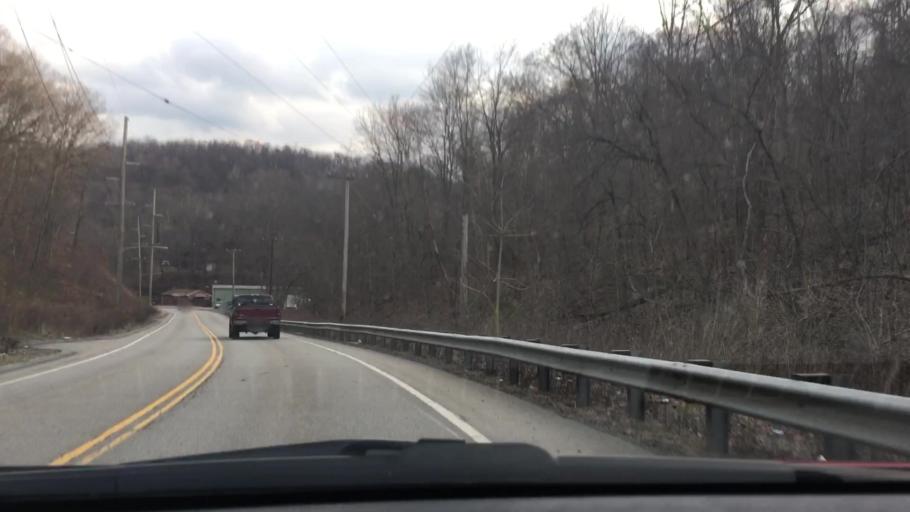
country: US
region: Pennsylvania
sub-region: Allegheny County
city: Glassport
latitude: 40.3257
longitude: -79.9108
